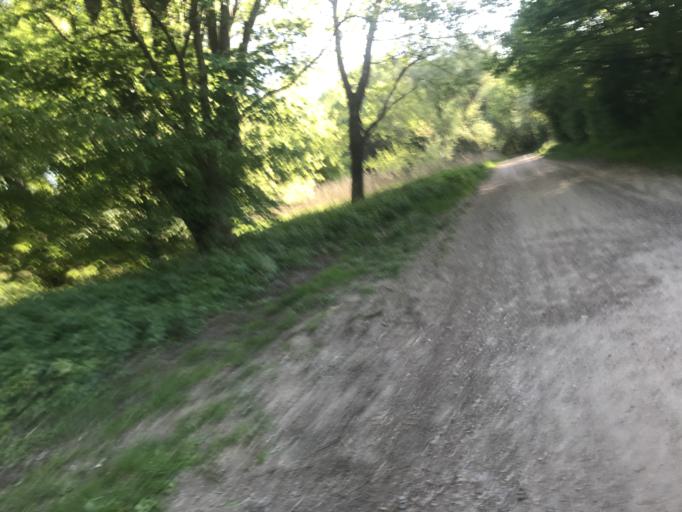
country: DE
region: Hesse
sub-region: Regierungsbezirk Darmstadt
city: Kiedrich
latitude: 50.0059
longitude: 8.0817
